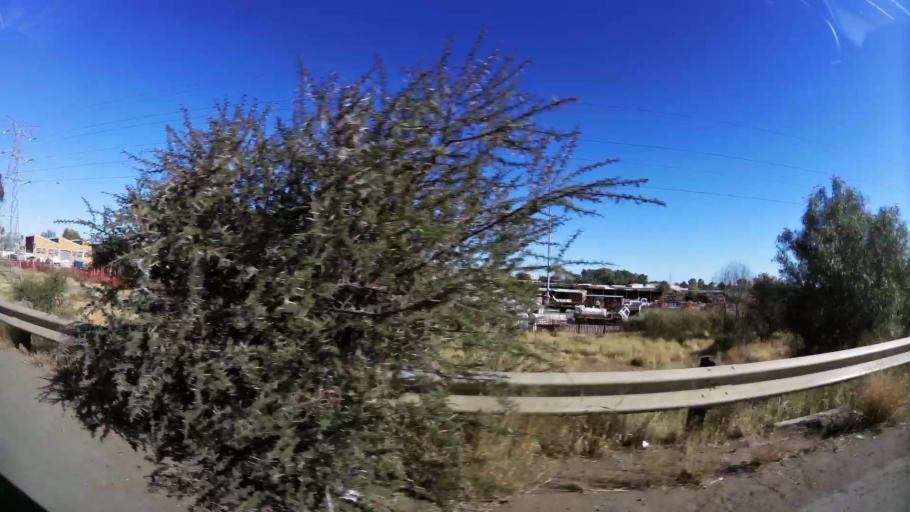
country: ZA
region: Northern Cape
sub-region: Frances Baard District Municipality
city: Kimberley
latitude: -28.7154
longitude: 24.7757
